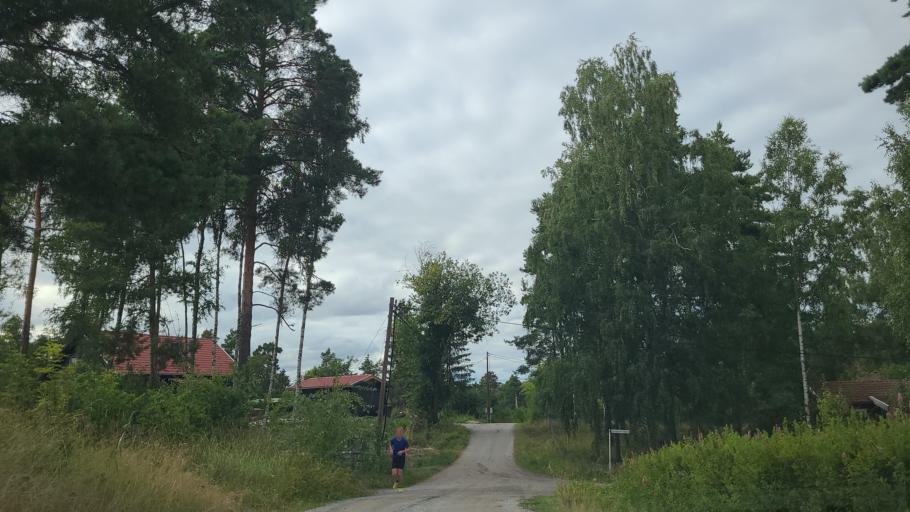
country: SE
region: Uppsala
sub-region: Habo Kommun
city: Balsta
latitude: 59.4760
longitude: 17.5488
